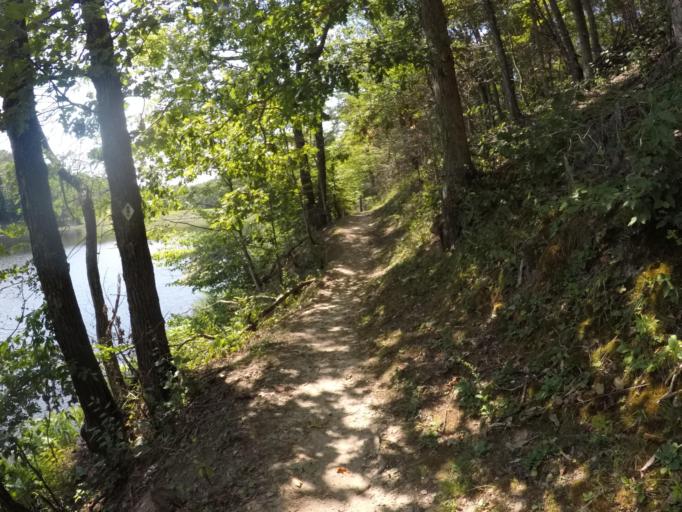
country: US
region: Ohio
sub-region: Lawrence County
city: Ironton
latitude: 38.6082
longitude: -82.6310
